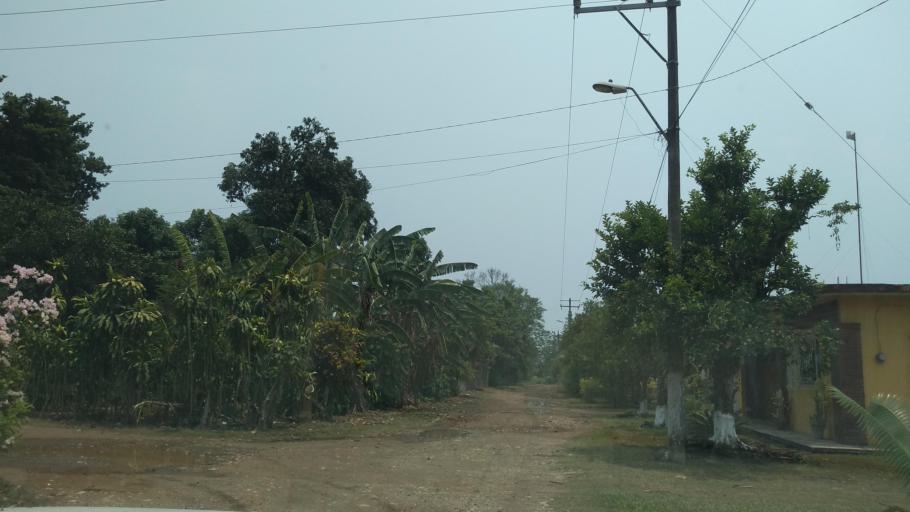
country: MX
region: Veracruz
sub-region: Tezonapa
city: Laguna Chica (Pueblo Nuevo)
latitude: 18.5135
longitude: -96.7383
